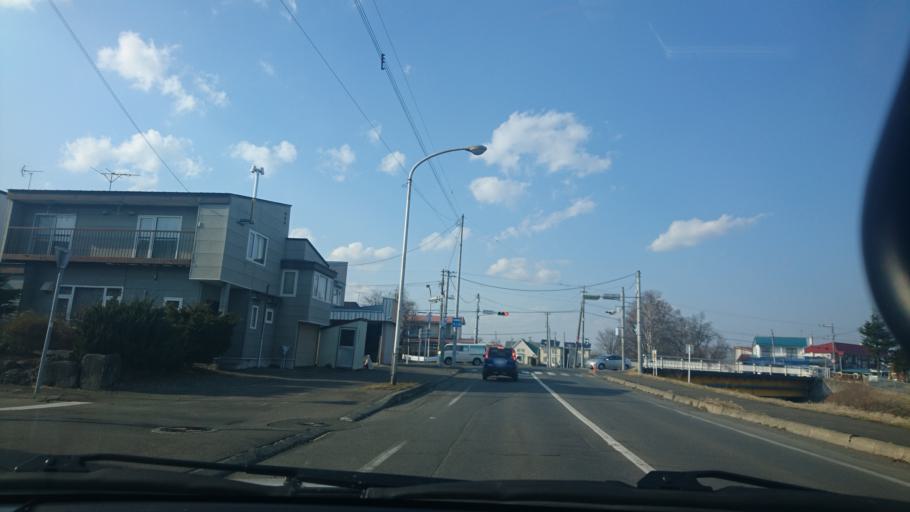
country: JP
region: Hokkaido
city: Obihiro
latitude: 42.9222
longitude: 143.1575
